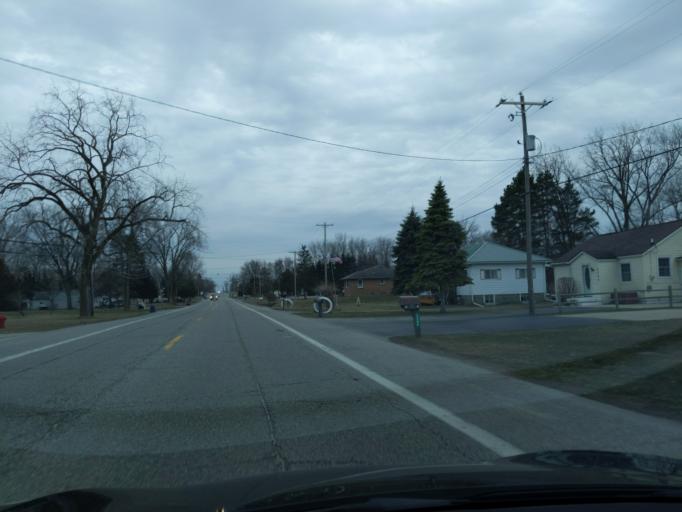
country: US
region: Michigan
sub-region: Bay County
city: Bay City
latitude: 43.6420
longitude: -83.9135
